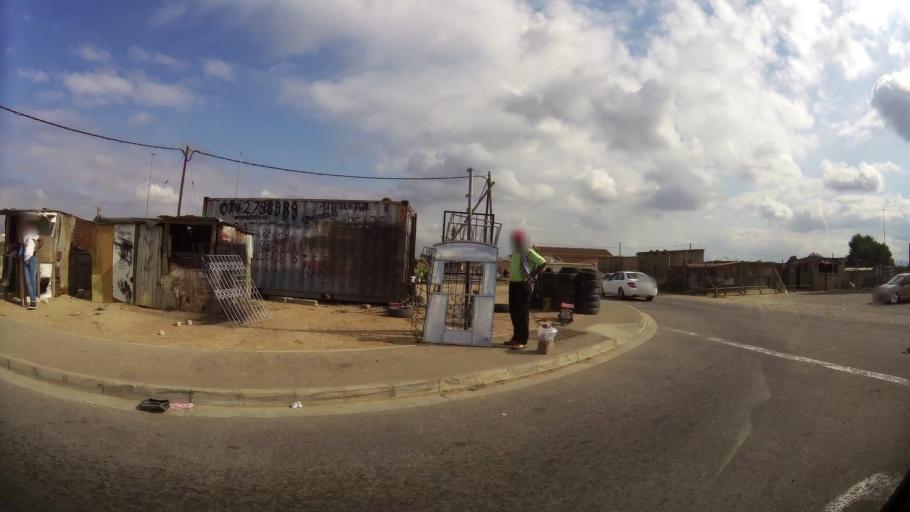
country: ZA
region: Eastern Cape
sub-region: Nelson Mandela Bay Metropolitan Municipality
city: Port Elizabeth
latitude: -33.7903
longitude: 25.5799
